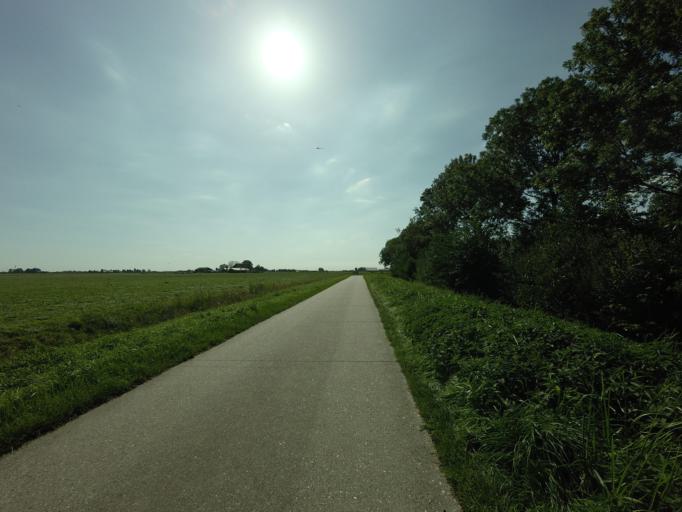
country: NL
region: Friesland
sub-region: Gemeente Littenseradiel
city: Makkum
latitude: 53.0942
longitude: 5.6438
